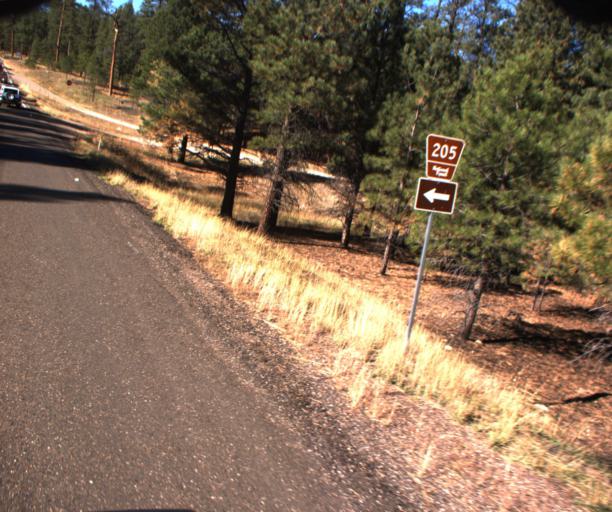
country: US
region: Arizona
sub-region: Coconino County
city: Fredonia
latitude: 36.7367
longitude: -112.1882
